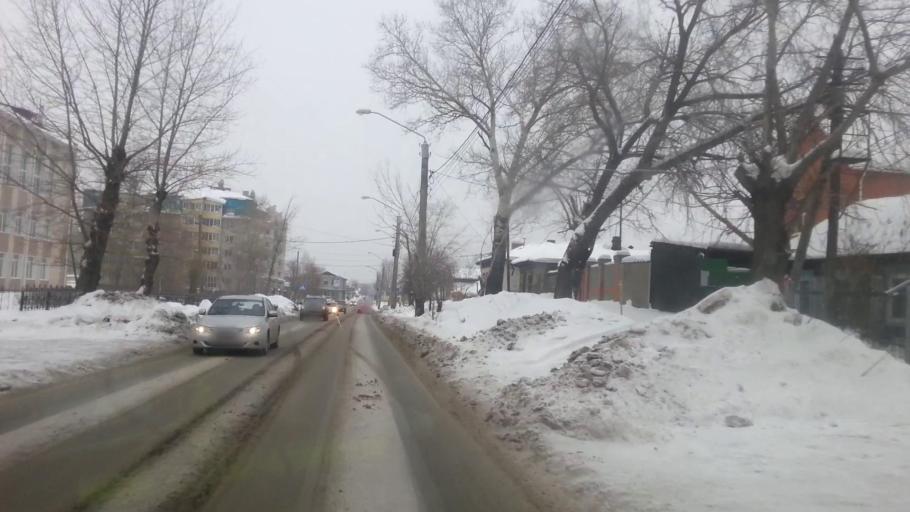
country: RU
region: Altai Krai
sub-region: Gorod Barnaulskiy
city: Barnaul
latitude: 53.3314
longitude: 83.7641
